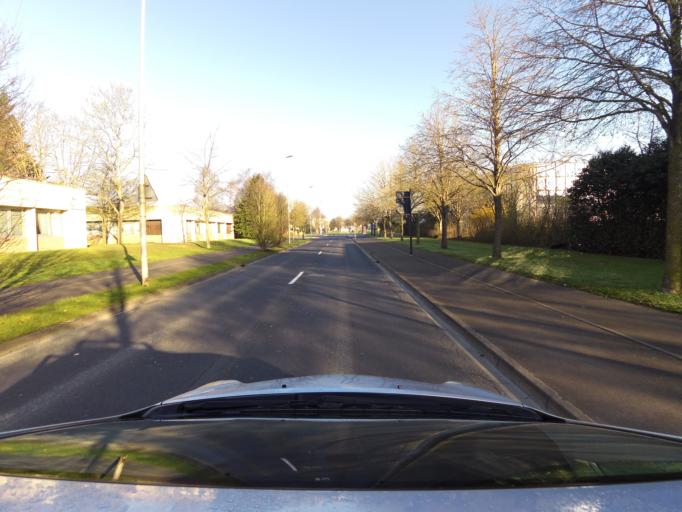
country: FR
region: Lower Normandy
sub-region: Departement du Calvados
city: Saint-Contest
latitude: 49.2016
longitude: -0.3892
